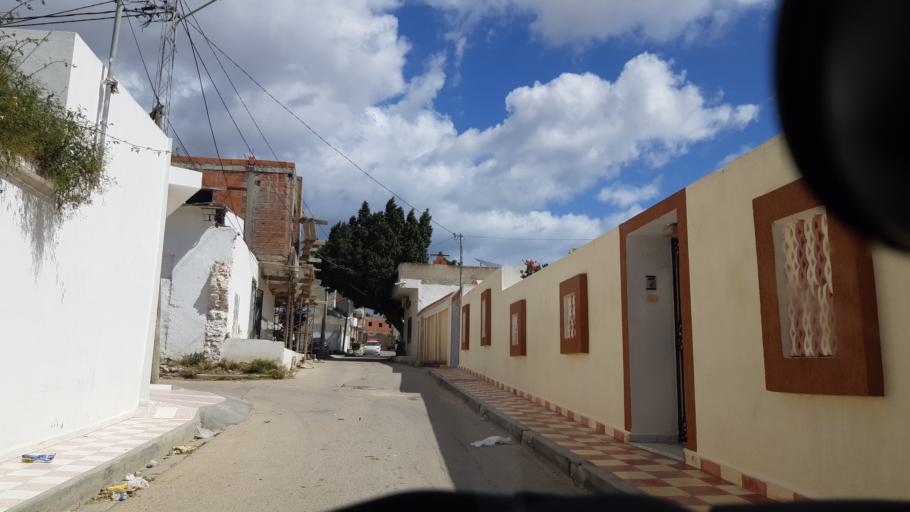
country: TN
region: Susah
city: Akouda
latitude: 35.8792
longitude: 10.5352
